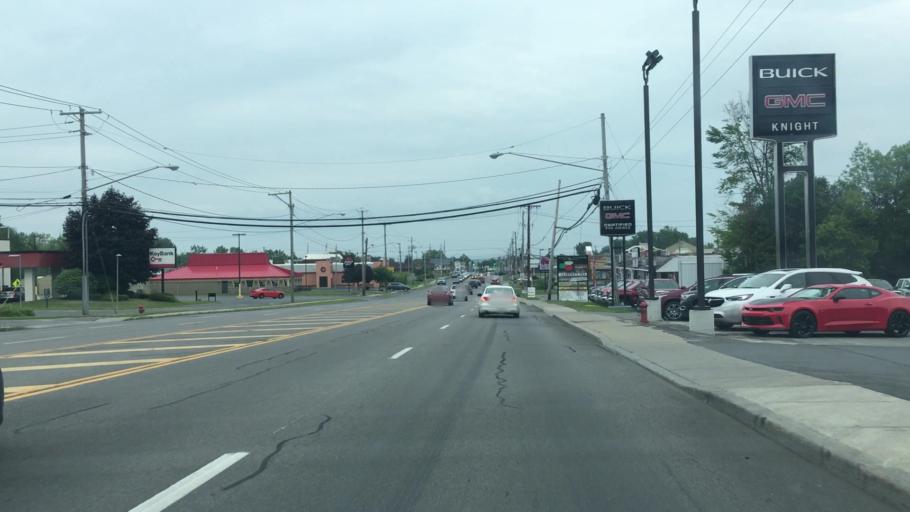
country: US
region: New York
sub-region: Clinton County
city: Plattsburgh West
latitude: 44.6968
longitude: -73.4864
